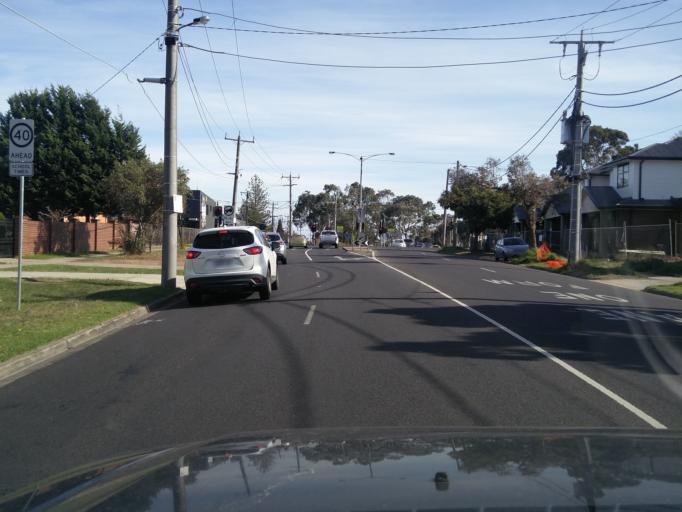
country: AU
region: Victoria
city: Macleod
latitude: -37.7298
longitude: 145.0619
